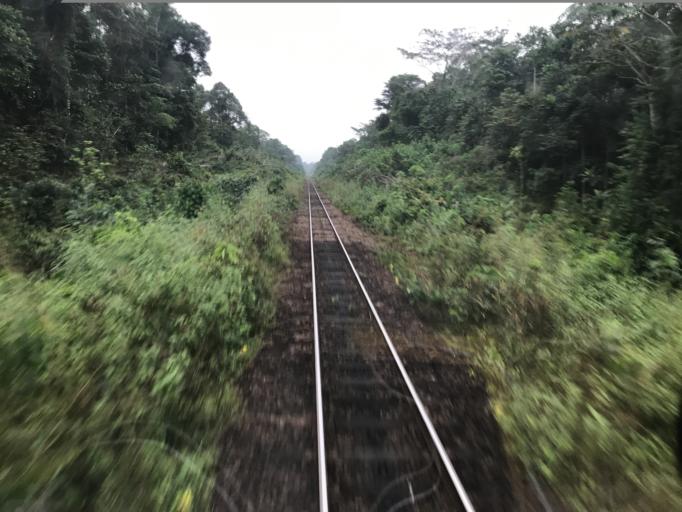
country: CM
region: Littoral
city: Edea
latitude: 3.9326
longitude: 10.1034
